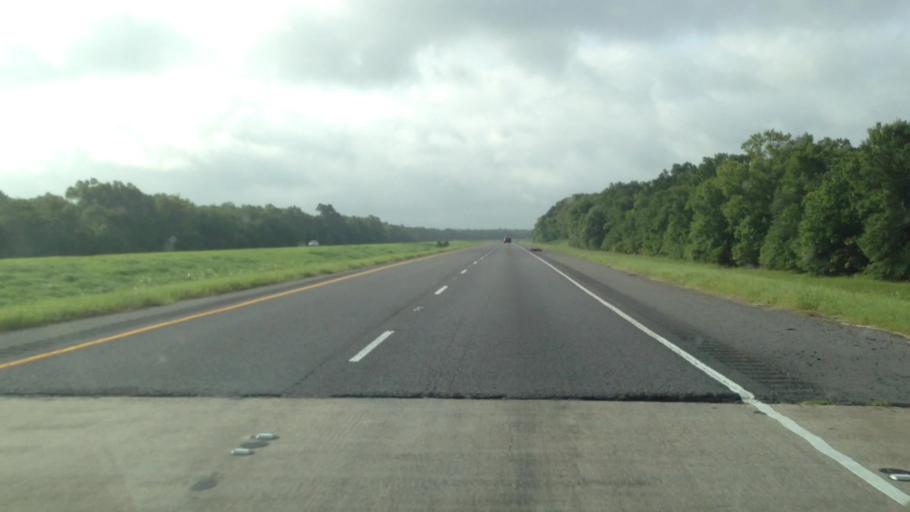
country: US
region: Louisiana
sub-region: Saint Landry Parish
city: Opelousas
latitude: 30.7042
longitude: -92.0929
